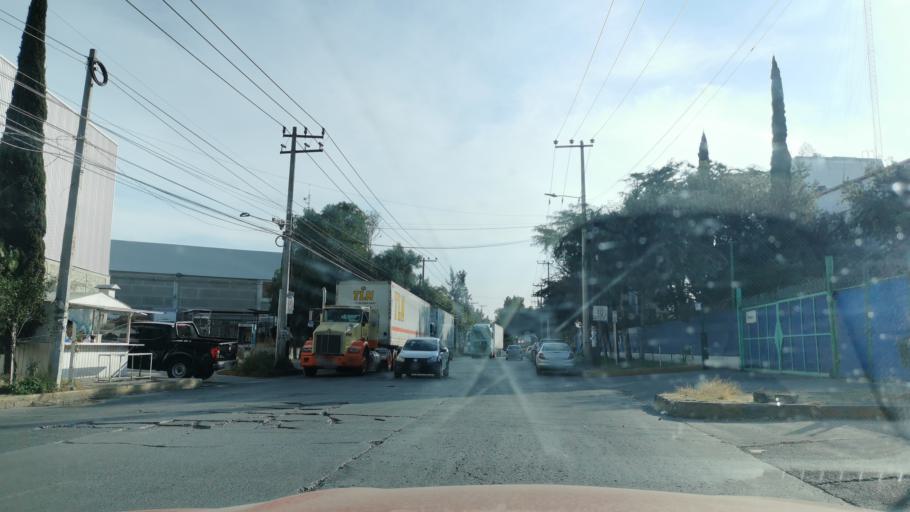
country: MX
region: Mexico
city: Cuautitlan
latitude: 19.6683
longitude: -99.2031
